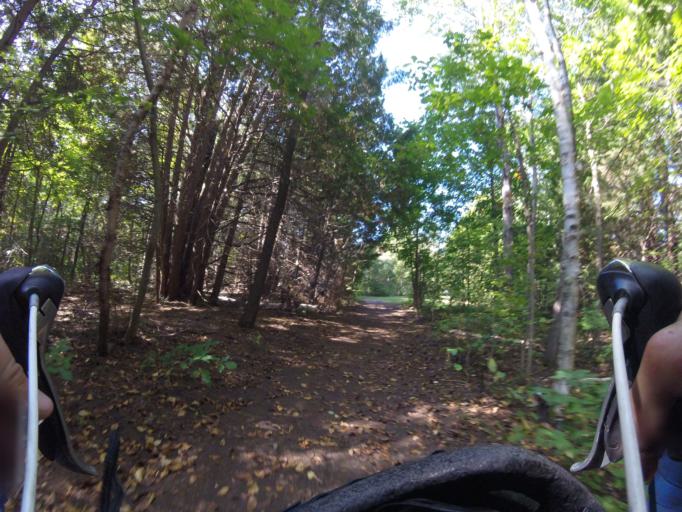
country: CA
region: Ontario
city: Bells Corners
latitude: 45.3051
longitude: -75.8924
